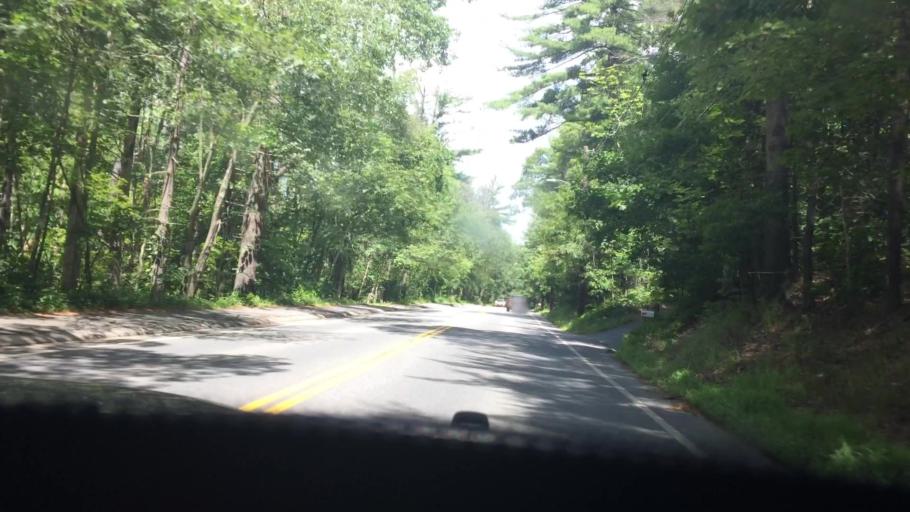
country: US
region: Massachusetts
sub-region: Middlesex County
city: Sudbury
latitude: 42.3883
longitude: -71.4195
